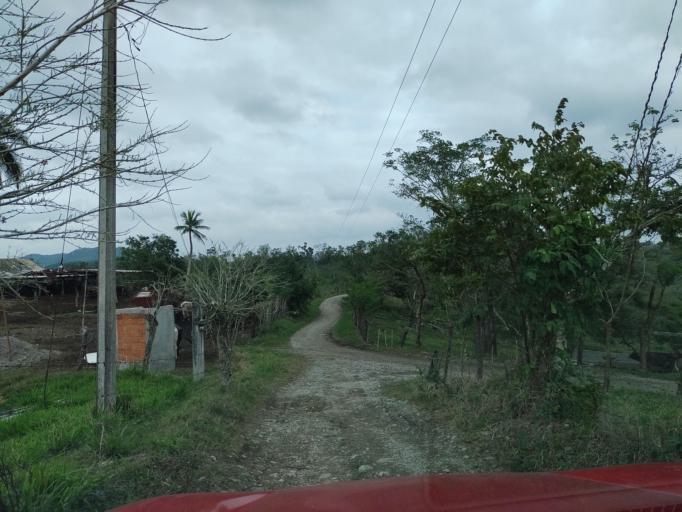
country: MX
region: Veracruz
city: Coatzintla
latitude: 20.4564
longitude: -97.4122
